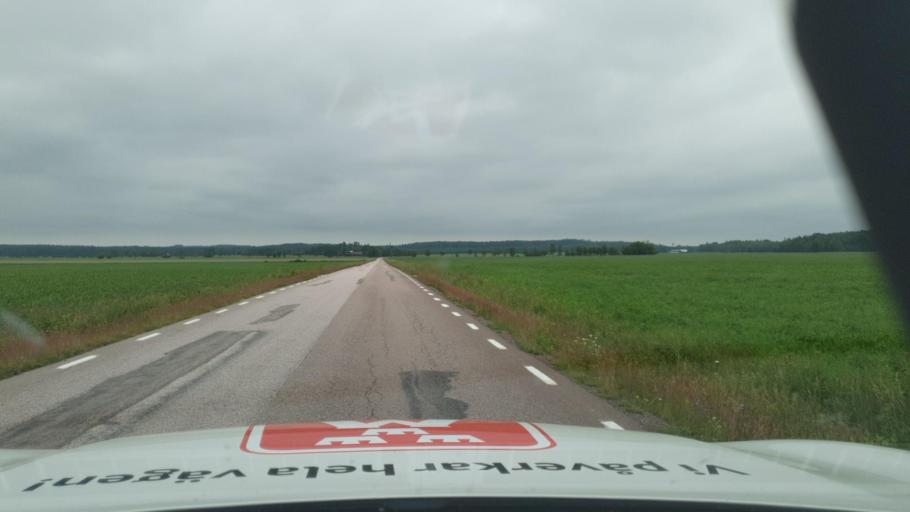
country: SE
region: Vaermland
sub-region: Karlstads Kommun
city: Skattkarr
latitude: 59.3973
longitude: 13.8601
